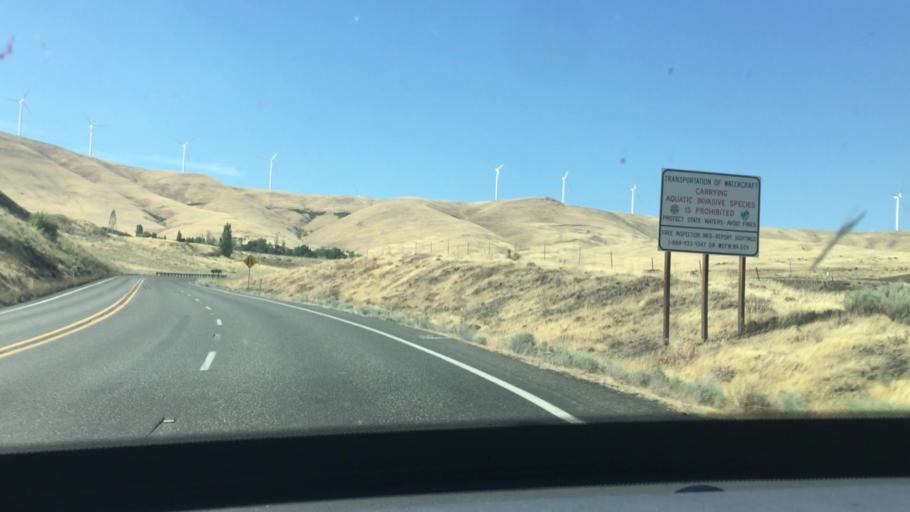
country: US
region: Washington
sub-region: Klickitat County
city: Goldendale
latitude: 45.6935
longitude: -120.8171
